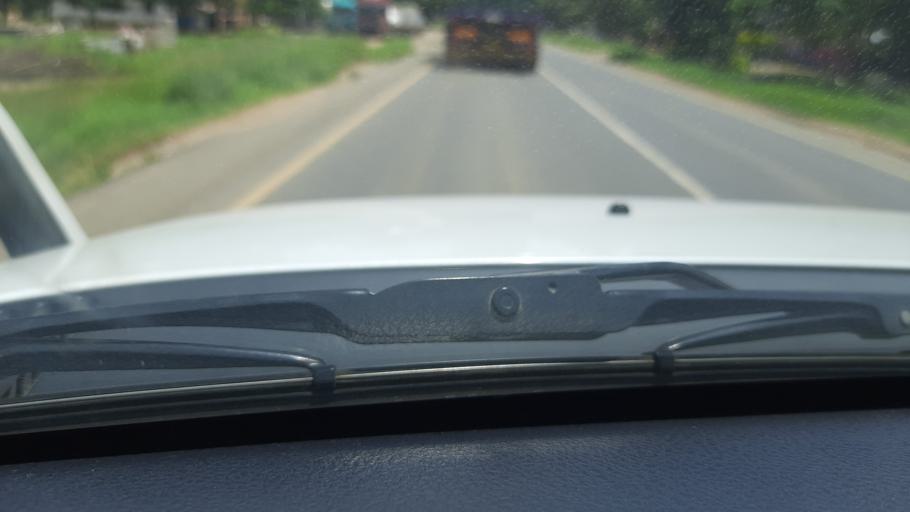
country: TZ
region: Pwani
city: Chalinze
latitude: -6.6380
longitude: 38.3457
